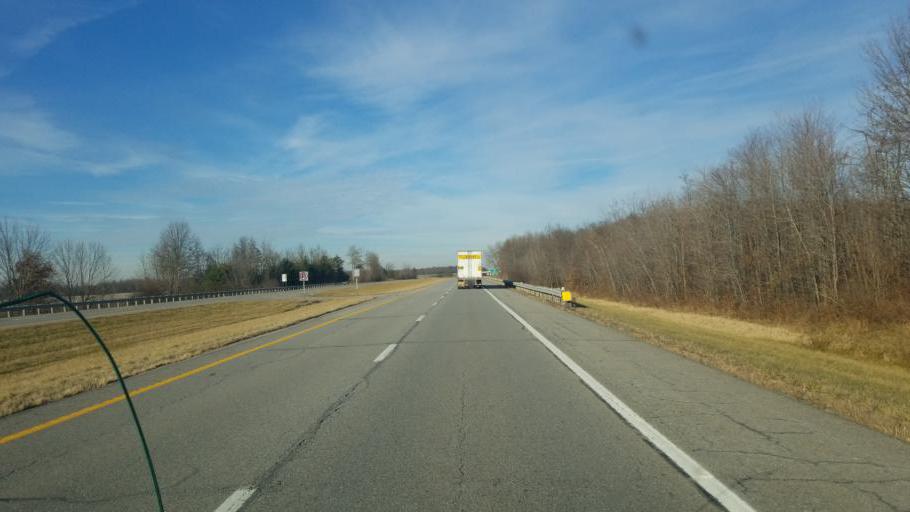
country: US
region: Ohio
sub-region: Trumbull County
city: Cortland
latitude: 41.4528
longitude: -80.7130
